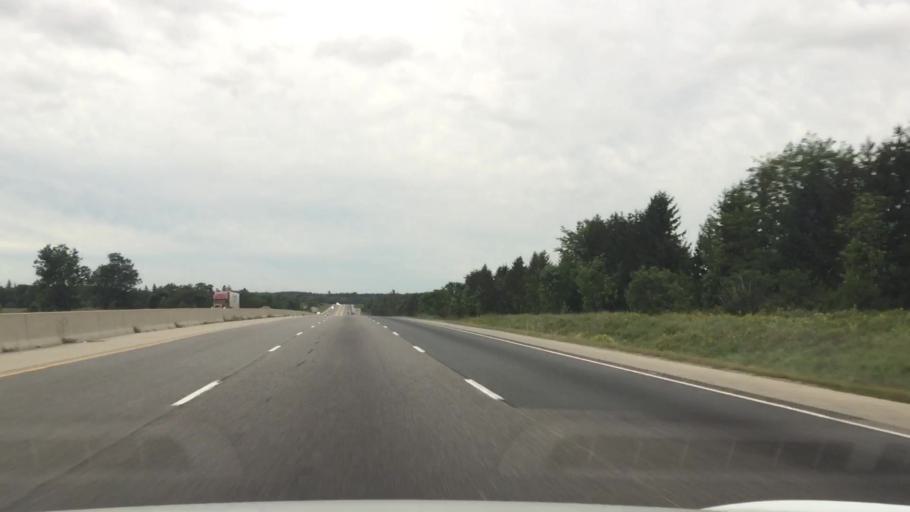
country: CA
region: Ontario
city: Kitchener
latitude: 43.2878
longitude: -80.5087
